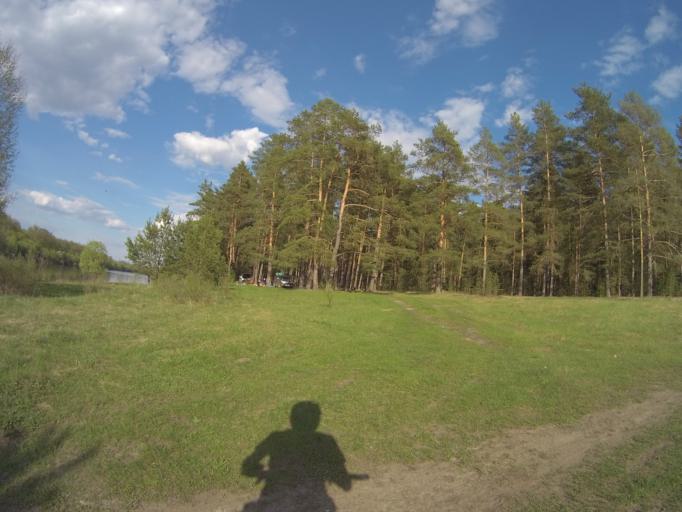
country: RU
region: Vladimir
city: Orgtrud
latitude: 56.1414
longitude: 40.7670
